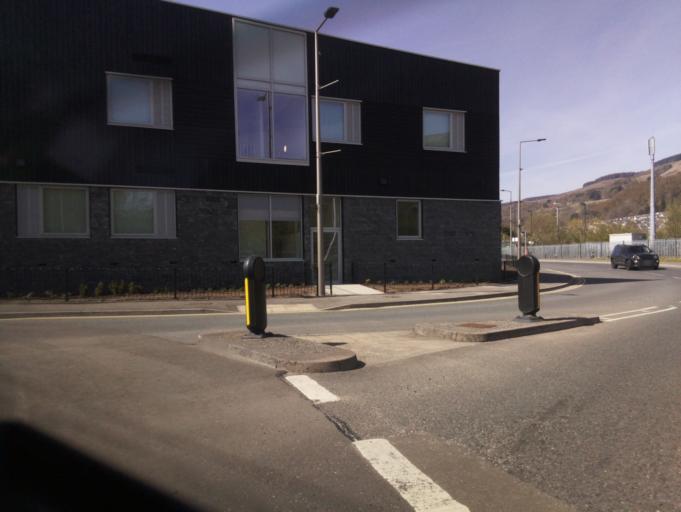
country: GB
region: Wales
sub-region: Rhondda Cynon Taf
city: Mountain Ash
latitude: 51.6808
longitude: -3.3755
